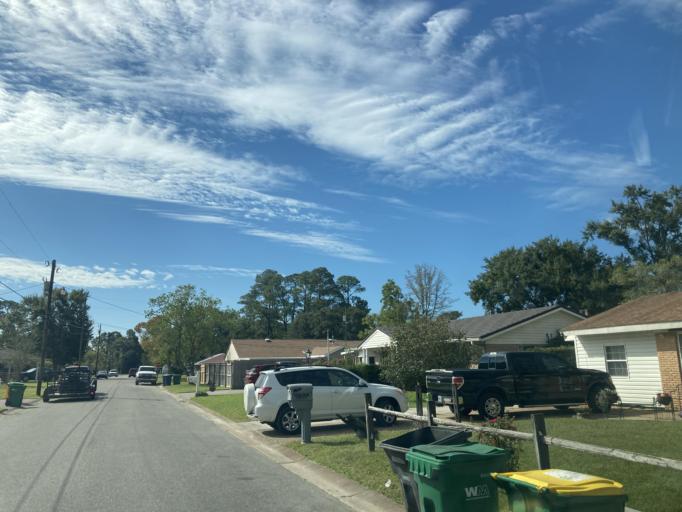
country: US
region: Mississippi
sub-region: Jackson County
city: Saint Martin
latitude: 30.4464
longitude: -88.8714
